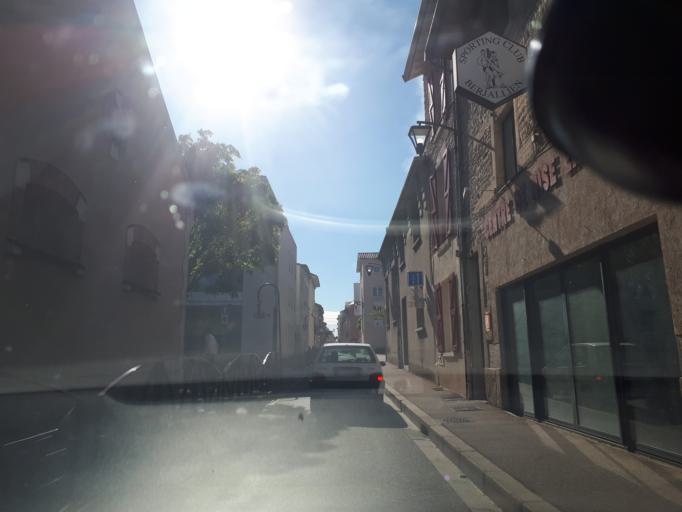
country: FR
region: Rhone-Alpes
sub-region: Departement de l'Isere
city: Bourgoin
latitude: 45.5865
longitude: 5.2802
